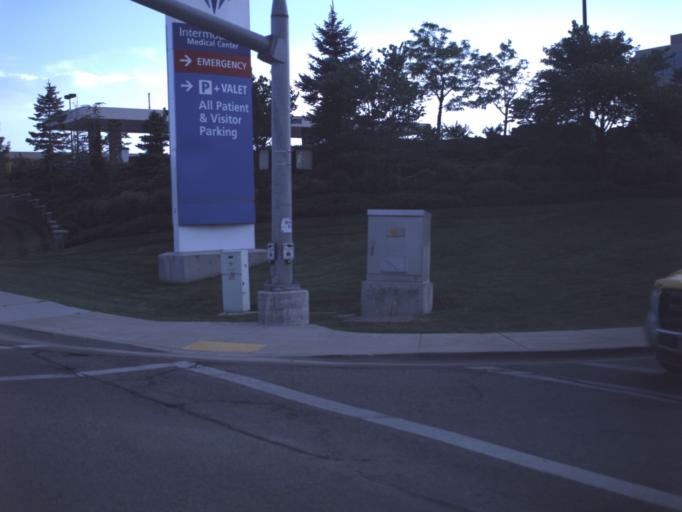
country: US
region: Utah
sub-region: Salt Lake County
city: Murray
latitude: 40.6594
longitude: -111.8884
